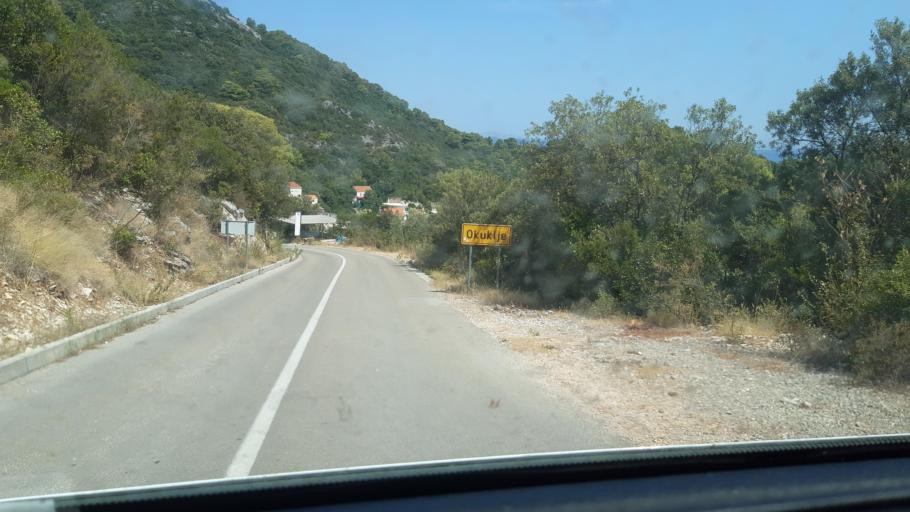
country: HR
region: Dubrovacko-Neretvanska
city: Ston
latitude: 42.7244
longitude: 17.6685
